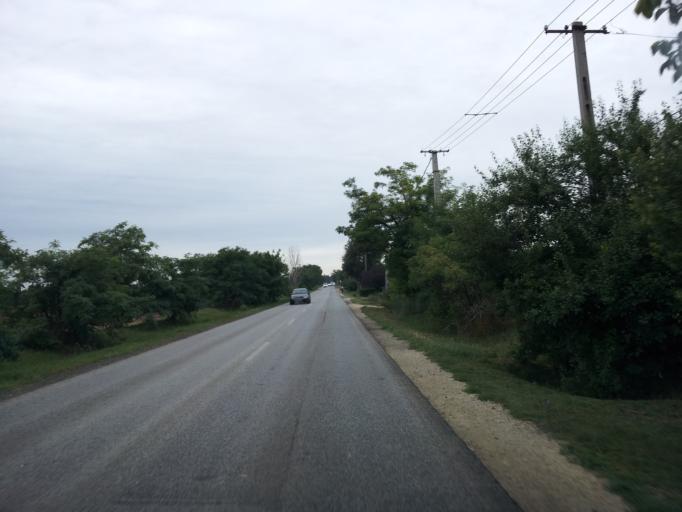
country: HU
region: Pest
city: Tarnok
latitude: 47.3849
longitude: 18.8611
